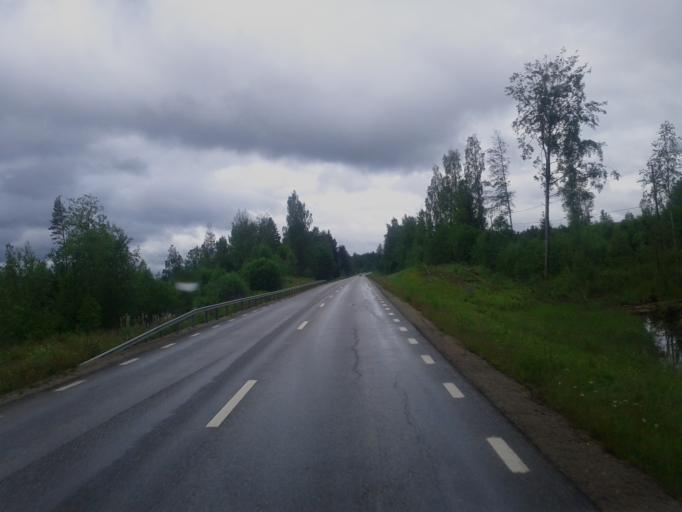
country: SE
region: Gaevleborg
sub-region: Nordanstigs Kommun
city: Bergsjoe
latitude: 62.0859
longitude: 16.7917
